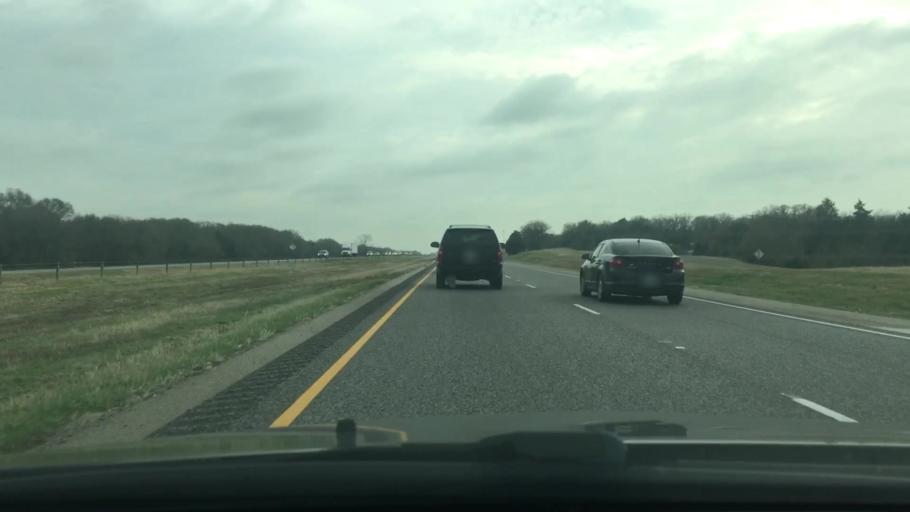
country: US
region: Texas
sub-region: Freestone County
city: Fairfield
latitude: 31.6251
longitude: -96.1577
